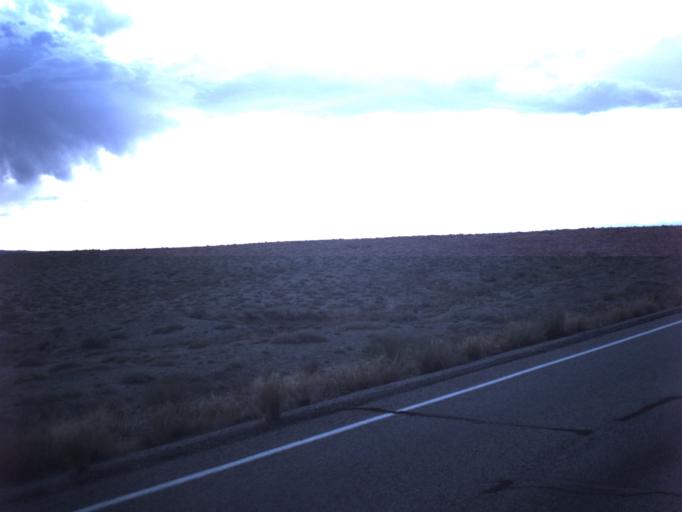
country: US
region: Utah
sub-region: Grand County
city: Moab
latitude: 38.9060
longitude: -109.3235
